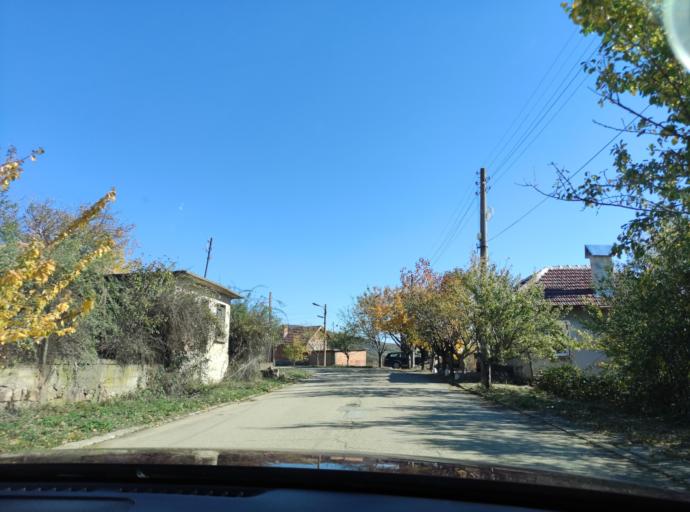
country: BG
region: Montana
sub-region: Obshtina Chiprovtsi
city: Chiprovtsi
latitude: 43.4558
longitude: 23.0366
